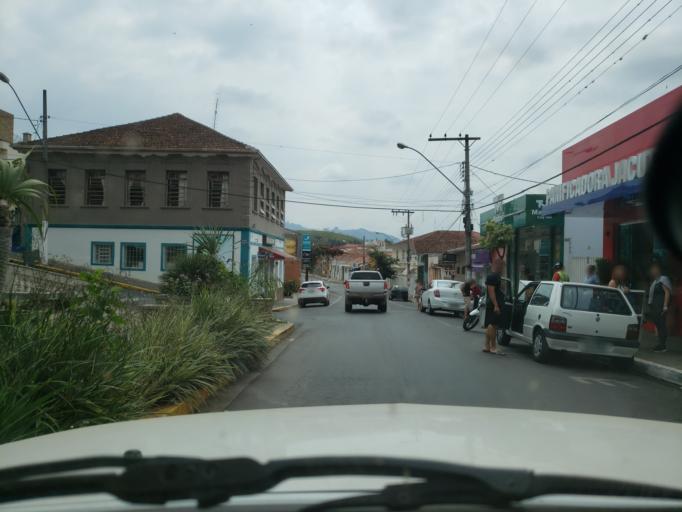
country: BR
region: Minas Gerais
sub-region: Jacutinga
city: Jacutinga
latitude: -22.2855
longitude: -46.6121
